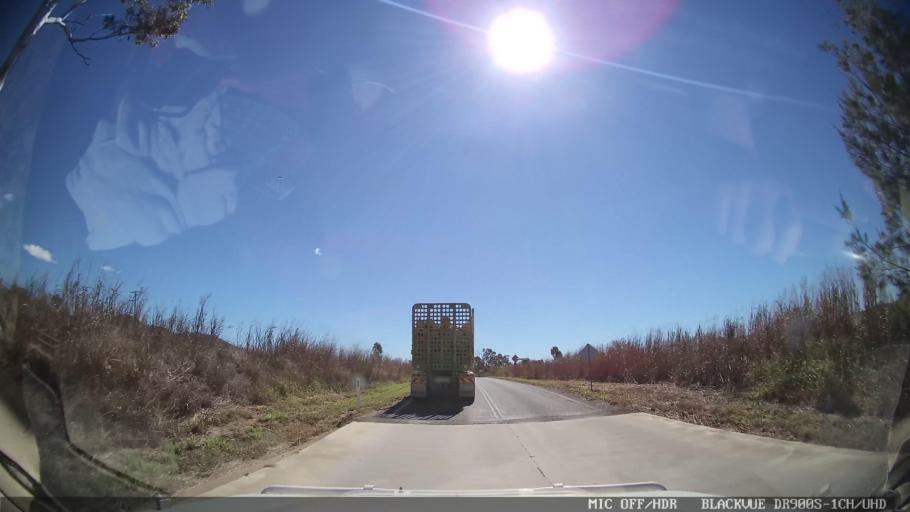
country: AU
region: Queensland
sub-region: Gladstone
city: Toolooa
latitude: -24.2721
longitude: 151.2755
